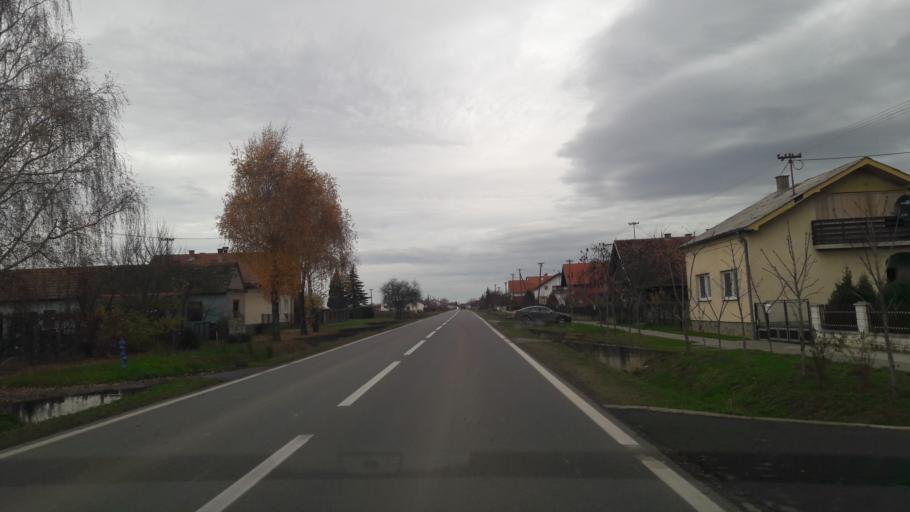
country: HR
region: Osjecko-Baranjska
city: Fericanci
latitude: 45.5289
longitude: 17.9549
